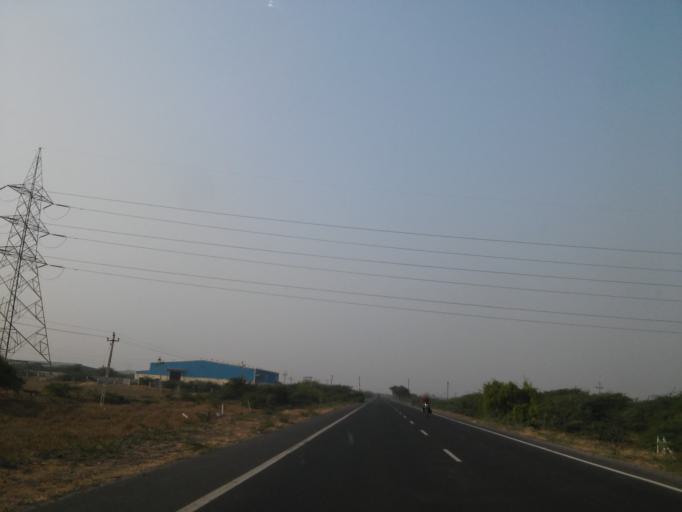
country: IN
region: Gujarat
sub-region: Kachchh
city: Anjar
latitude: 23.3013
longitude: 70.1059
